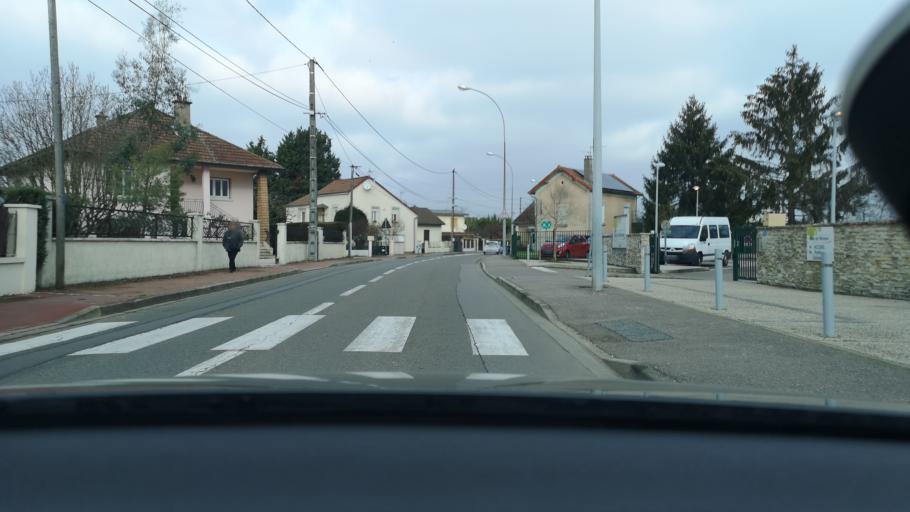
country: FR
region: Bourgogne
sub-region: Departement de Saone-et-Loire
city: Chalon-sur-Saone
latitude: 46.8020
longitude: 4.8508
